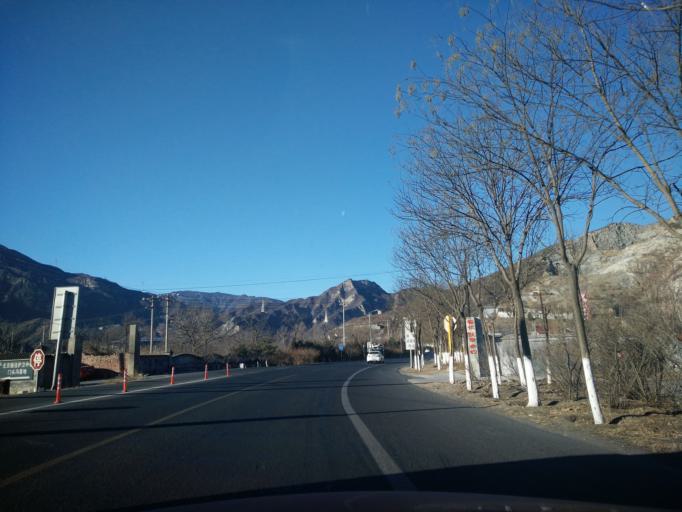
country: CN
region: Beijing
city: Miaofengshan
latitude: 39.9792
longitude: 116.0585
